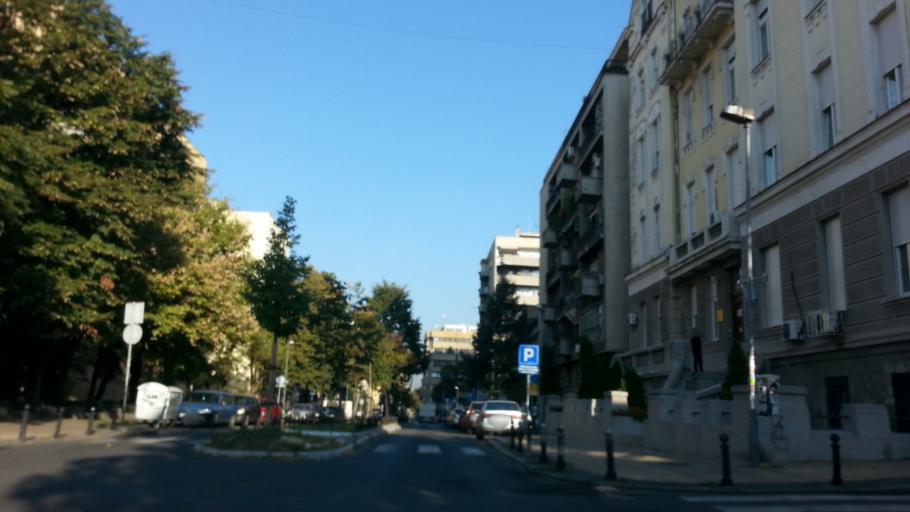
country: RS
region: Central Serbia
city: Belgrade
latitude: 44.8045
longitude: 20.4714
